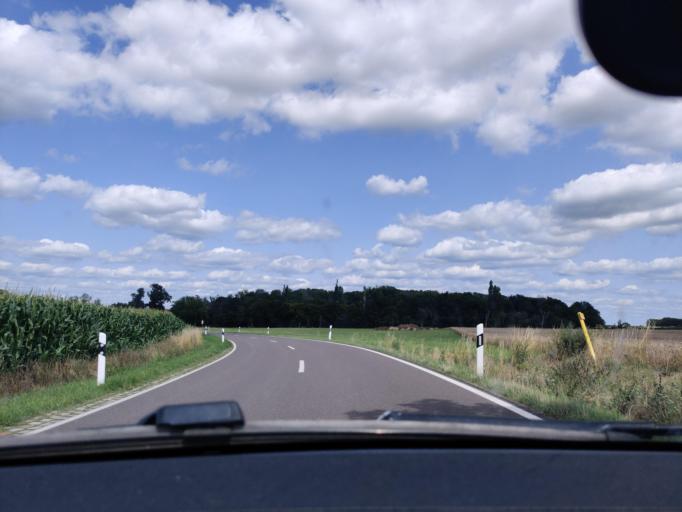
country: DE
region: Saxony-Anhalt
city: Leitzkau
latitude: 52.0726
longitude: 12.0109
